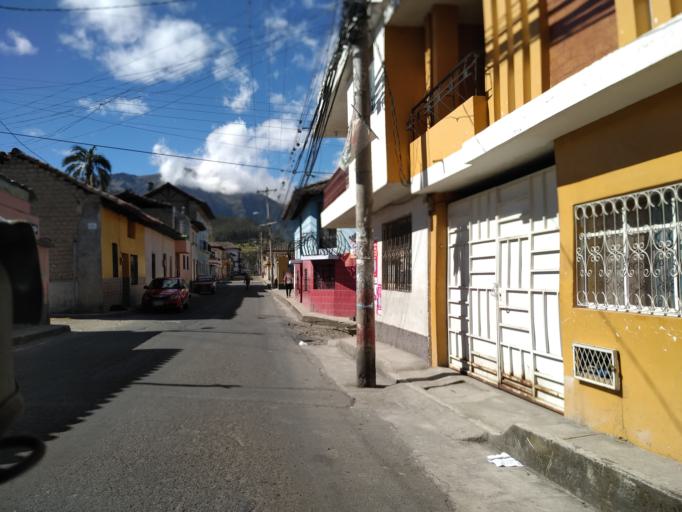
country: EC
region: Imbabura
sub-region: Canton Otavalo
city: Otavalo
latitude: 0.1979
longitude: -78.1917
